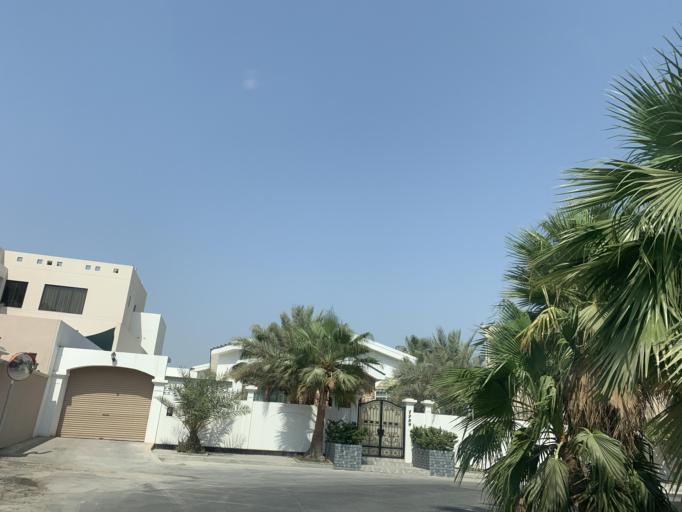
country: BH
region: Manama
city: Jidd Hafs
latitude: 26.2060
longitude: 50.5228
